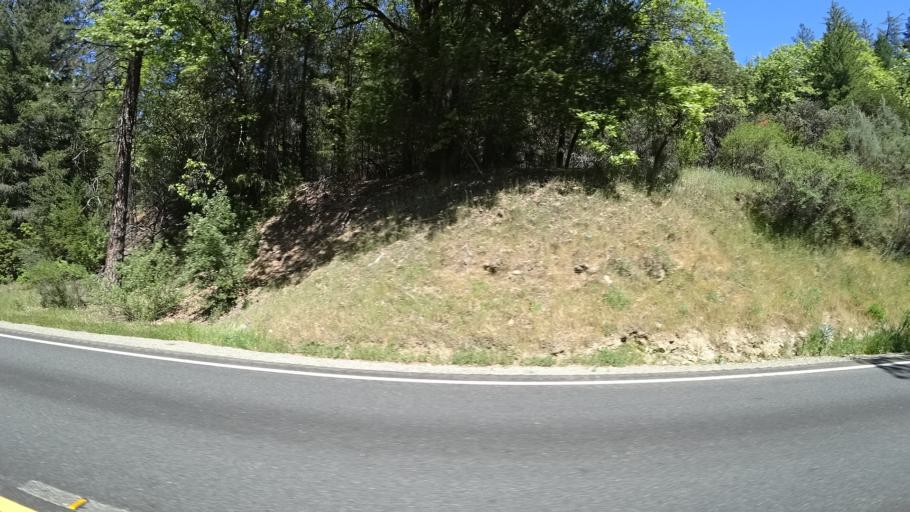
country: US
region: California
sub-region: Trinity County
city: Weaverville
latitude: 40.7395
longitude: -123.0611
